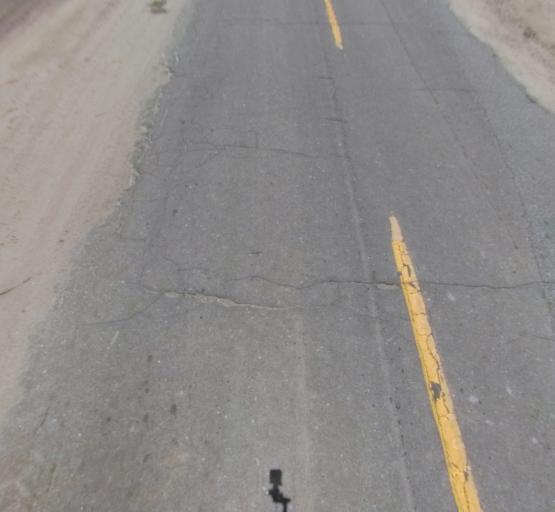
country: US
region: California
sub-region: Madera County
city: Chowchilla
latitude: 37.0512
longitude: -120.2925
